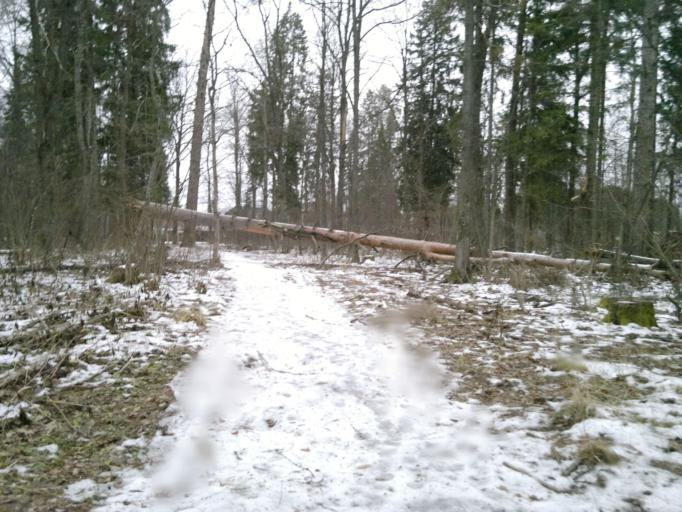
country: RU
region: Mariy-El
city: Yoshkar-Ola
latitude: 56.6139
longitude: 47.9450
